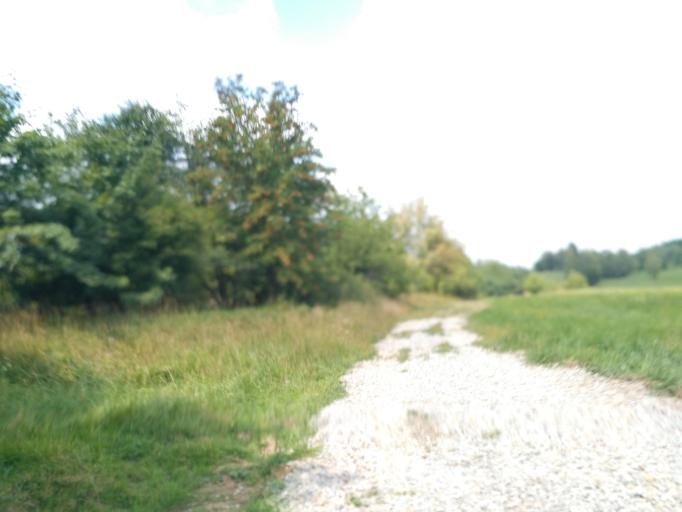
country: PL
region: Subcarpathian Voivodeship
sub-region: Powiat krosnienski
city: Iwonicz-Zdroj
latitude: 49.5735
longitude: 21.8094
